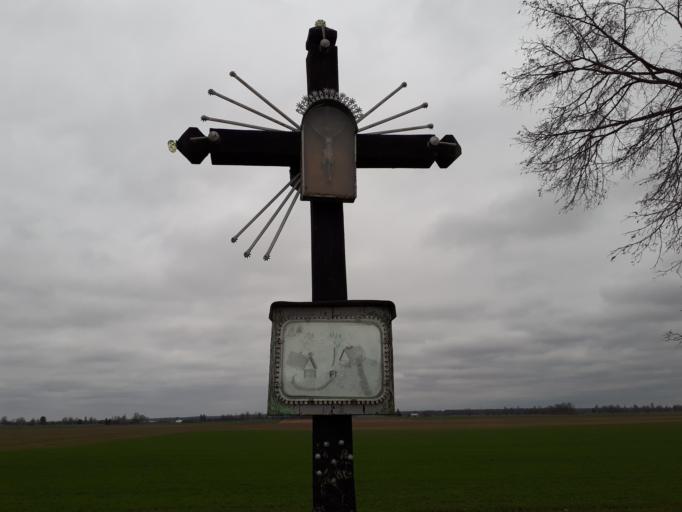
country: LT
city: Jieznas
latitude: 54.5428
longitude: 24.2074
